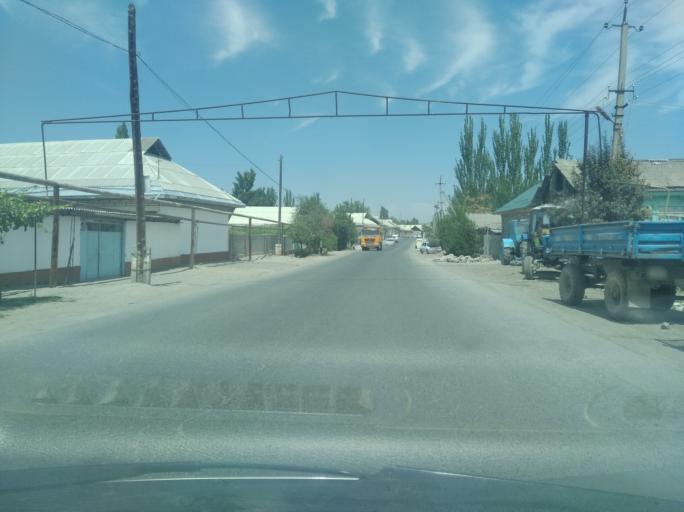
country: KG
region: Osh
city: Aravan
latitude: 40.6223
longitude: 72.4512
